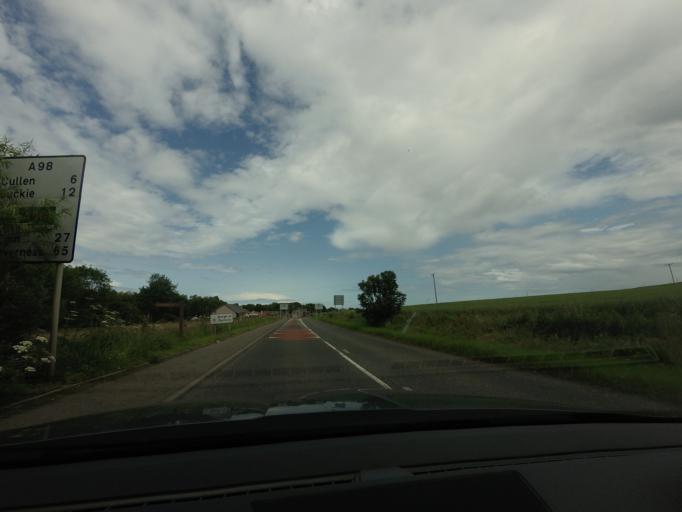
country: GB
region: Scotland
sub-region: Aberdeenshire
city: Portsoy
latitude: 57.6751
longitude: -2.6879
